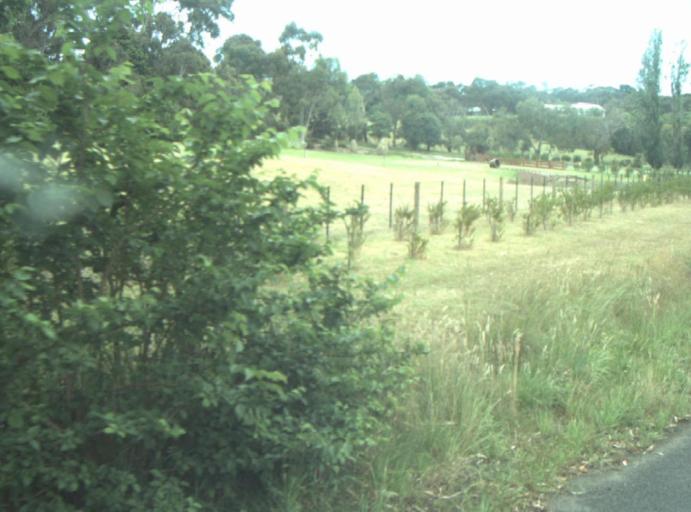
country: AU
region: Victoria
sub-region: Greater Geelong
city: Leopold
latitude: -38.2127
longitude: 144.5072
